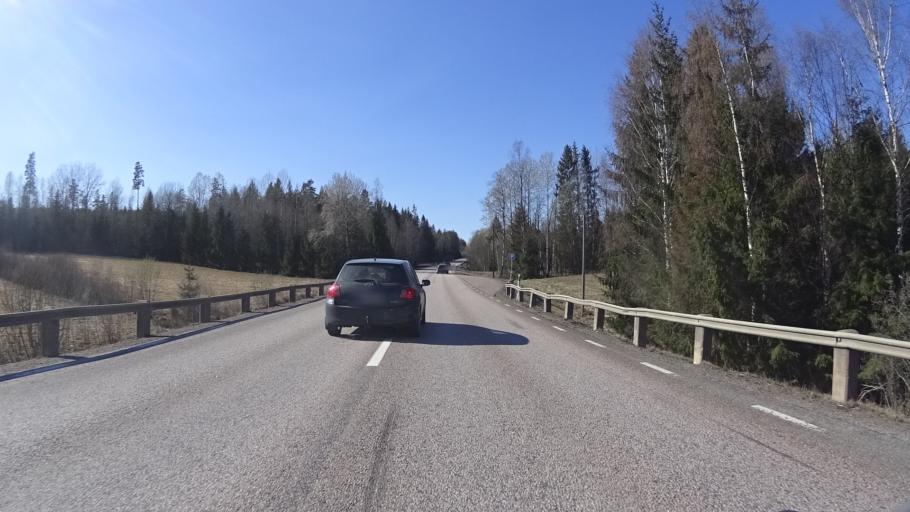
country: SE
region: Vaermland
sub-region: Karlstads Kommun
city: Edsvalla
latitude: 59.5413
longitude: 13.0842
